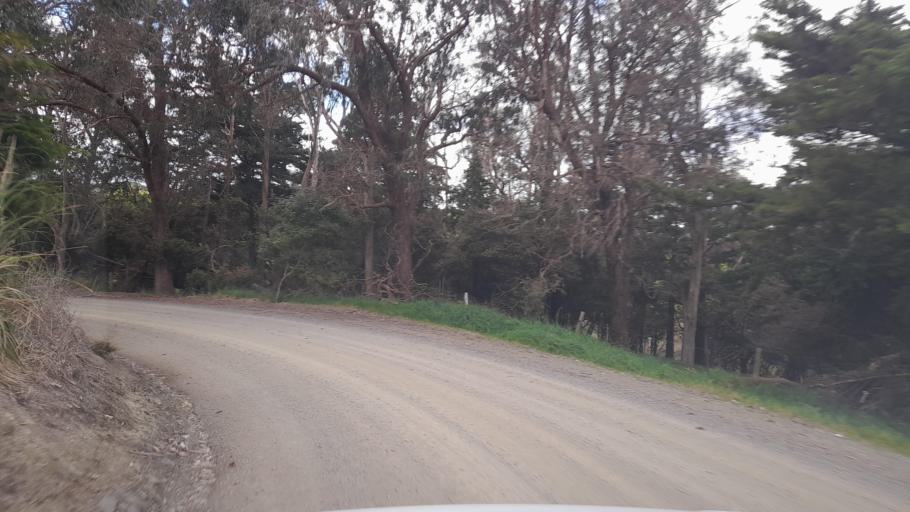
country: NZ
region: Auckland
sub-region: Auckland
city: Wellsford
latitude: -36.1933
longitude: 174.3272
